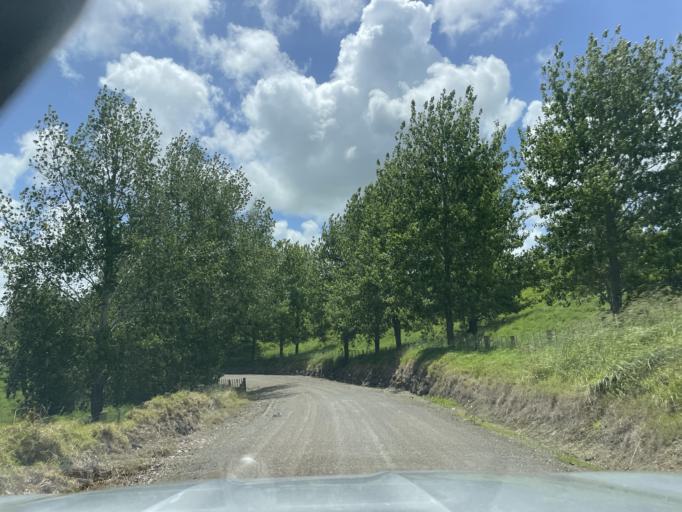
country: NZ
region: Auckland
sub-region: Auckland
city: Wellsford
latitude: -36.1902
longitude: 174.3255
